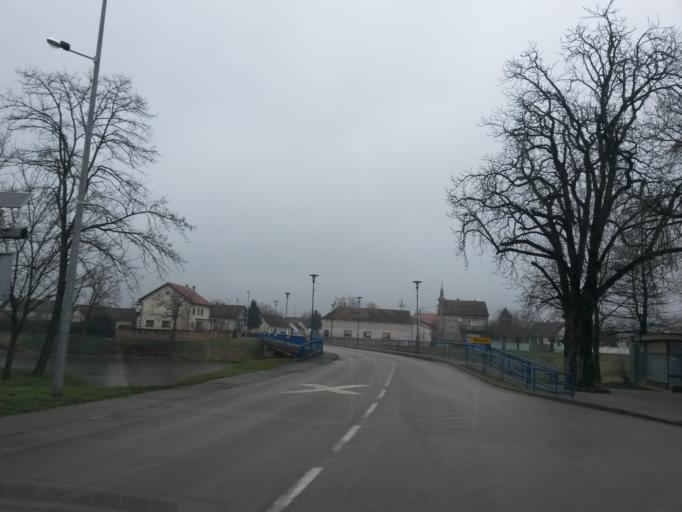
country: HR
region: Vukovarsko-Srijemska
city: Andrijasevci
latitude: 45.2266
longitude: 18.7417
